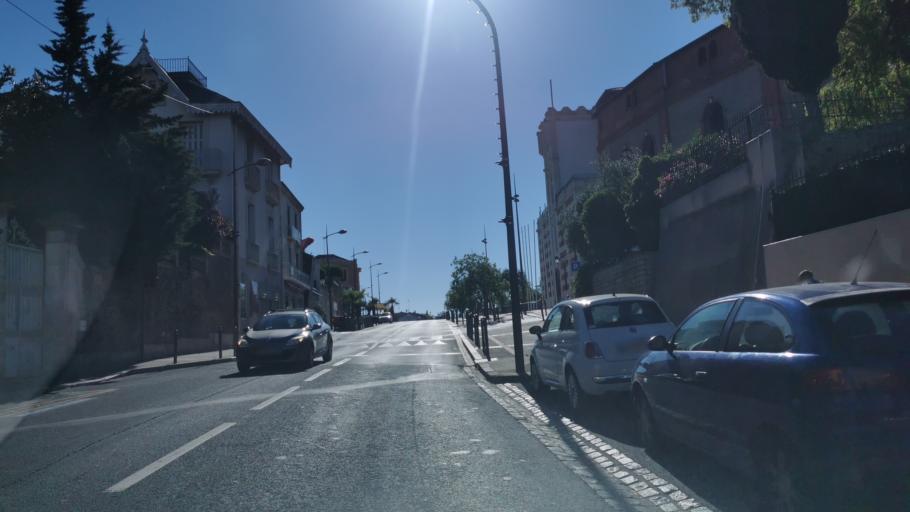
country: FR
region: Languedoc-Roussillon
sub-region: Departement de l'Herault
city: Beziers
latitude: 43.3440
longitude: 3.2279
